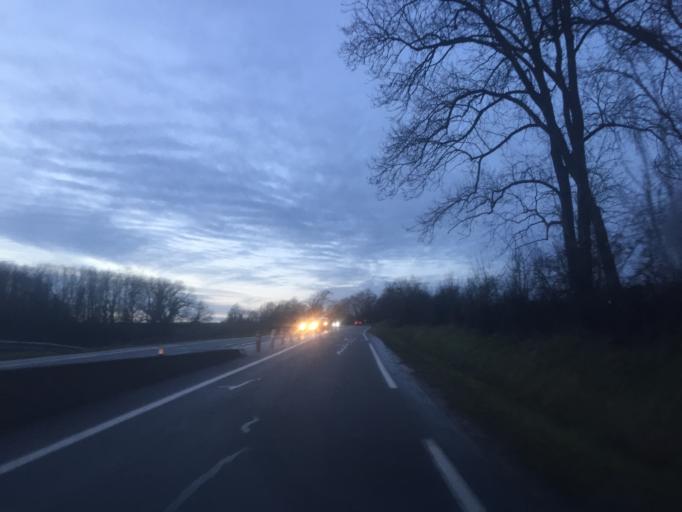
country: FR
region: Franche-Comte
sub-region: Departement du Jura
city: Orchamps
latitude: 47.1359
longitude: 5.5801
